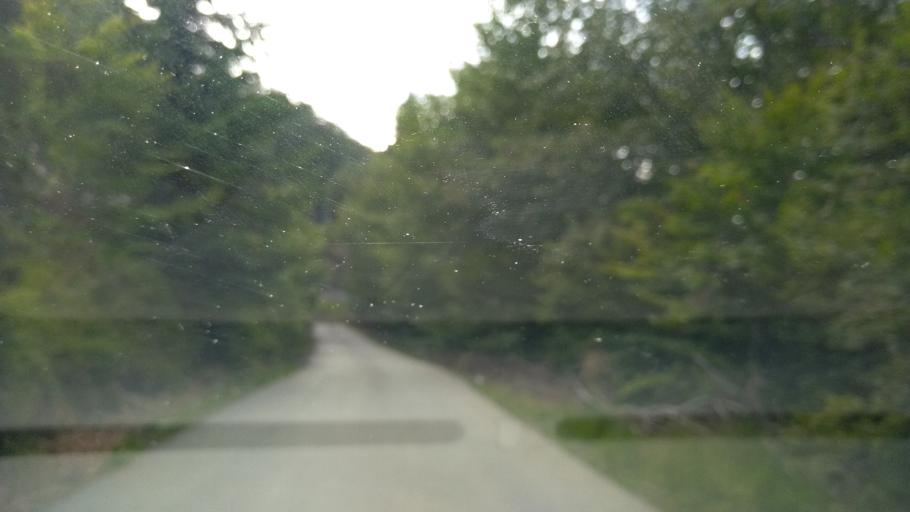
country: RO
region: Hunedoara
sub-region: Municipiul  Vulcan
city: Jiu-Paroseni
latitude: 45.3204
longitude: 23.2957
